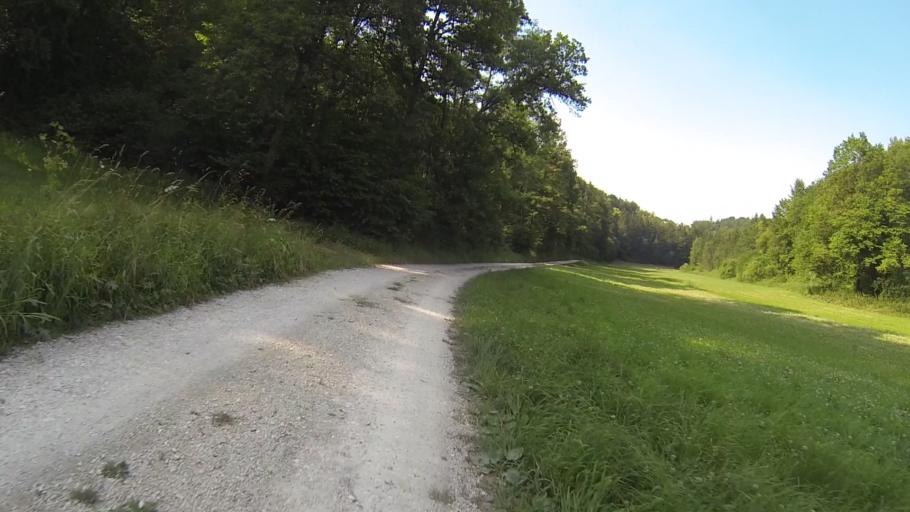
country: DE
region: Baden-Wuerttemberg
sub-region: Tuebingen Region
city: Dornstadt
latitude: 48.4339
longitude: 9.9038
